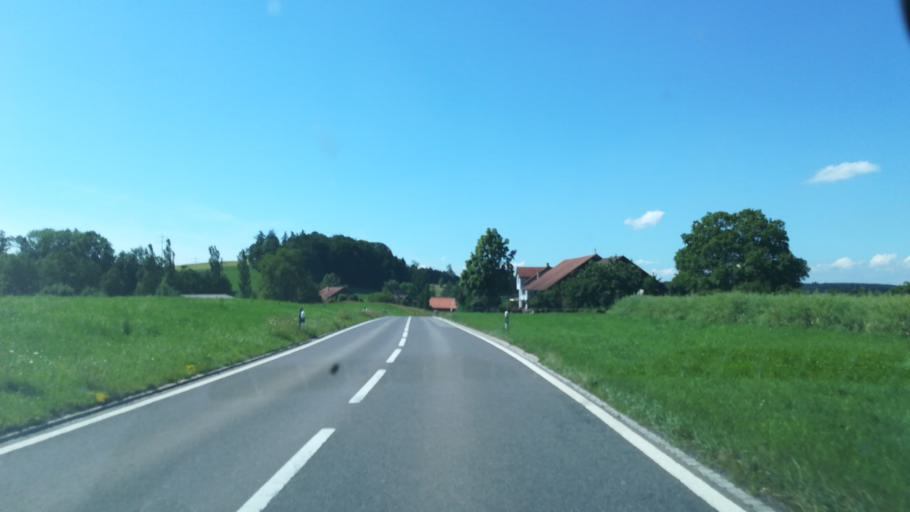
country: CH
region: Saint Gallen
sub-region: Wahlkreis St. Gallen
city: Andwil
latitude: 47.4573
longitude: 9.2510
